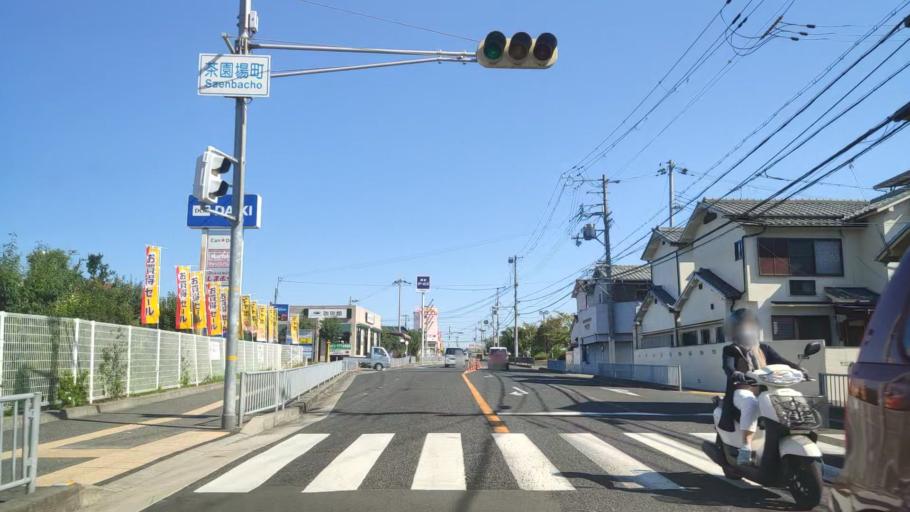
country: JP
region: Hyogo
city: Akashi
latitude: 34.6554
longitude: 134.9888
